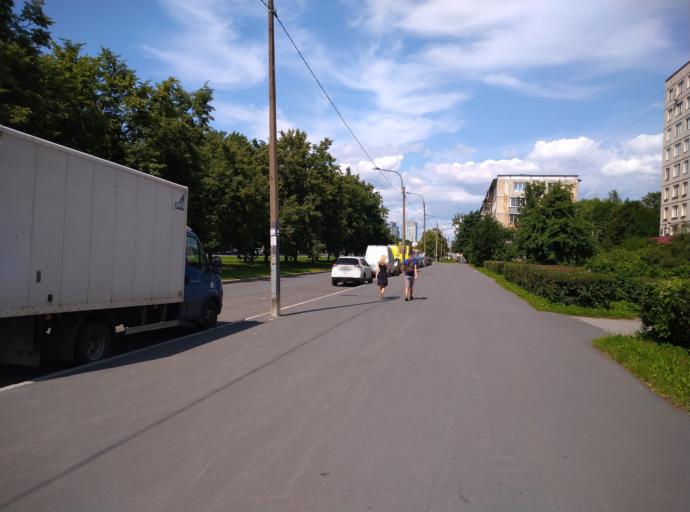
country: RU
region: St.-Petersburg
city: Kupchino
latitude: 59.8624
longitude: 30.3378
